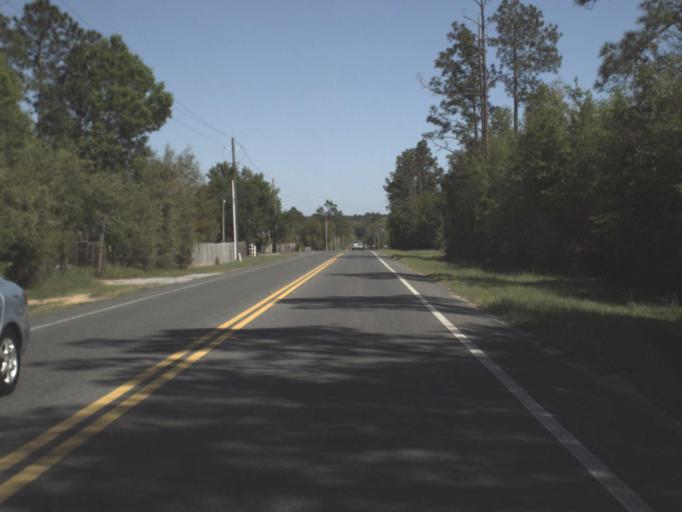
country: US
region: Florida
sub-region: Escambia County
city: Bellview
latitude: 30.5015
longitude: -87.3457
